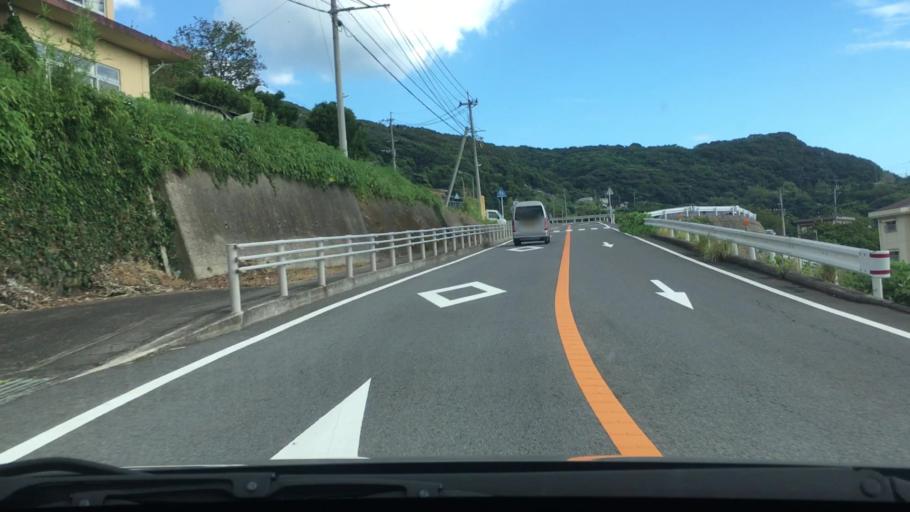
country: JP
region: Nagasaki
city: Togitsu
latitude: 32.8299
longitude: 129.7236
